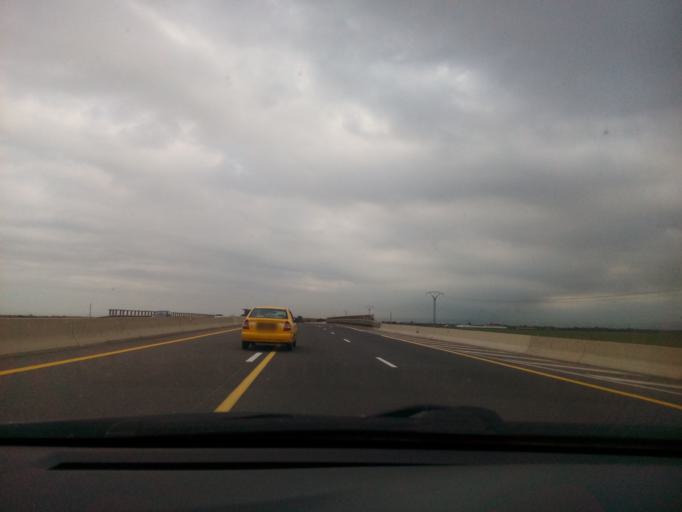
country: DZ
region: Relizane
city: Relizane
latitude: 35.7921
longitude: 0.4823
